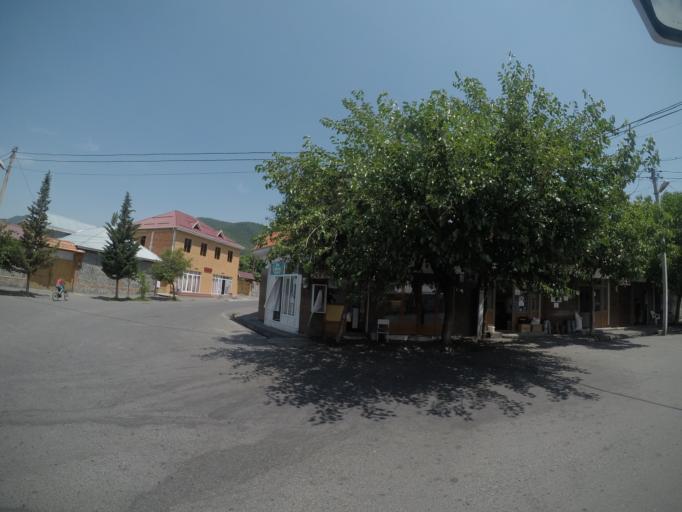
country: AZ
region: Qakh Rayon
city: Qax
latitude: 41.4163
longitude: 46.9202
